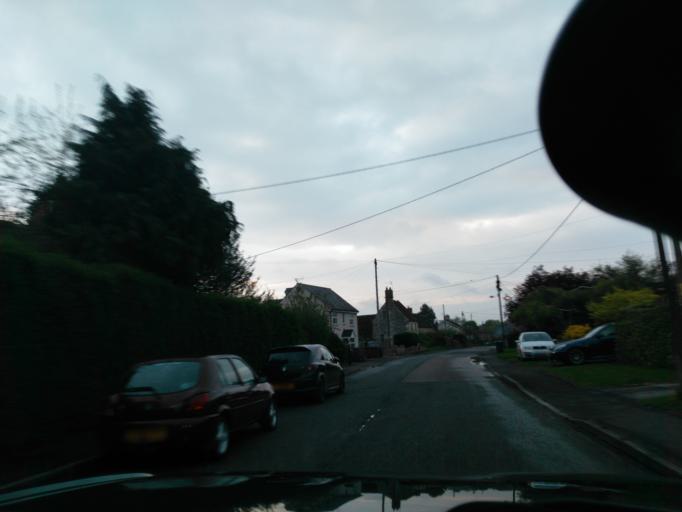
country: GB
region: England
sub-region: Wiltshire
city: Melksham
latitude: 51.3573
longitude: -2.1438
